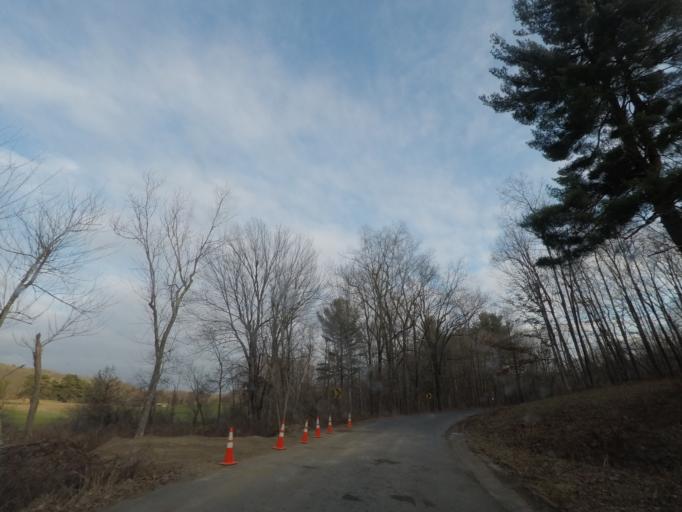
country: US
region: New York
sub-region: Rensselaer County
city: Wynantskill
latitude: 42.7212
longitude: -73.6364
